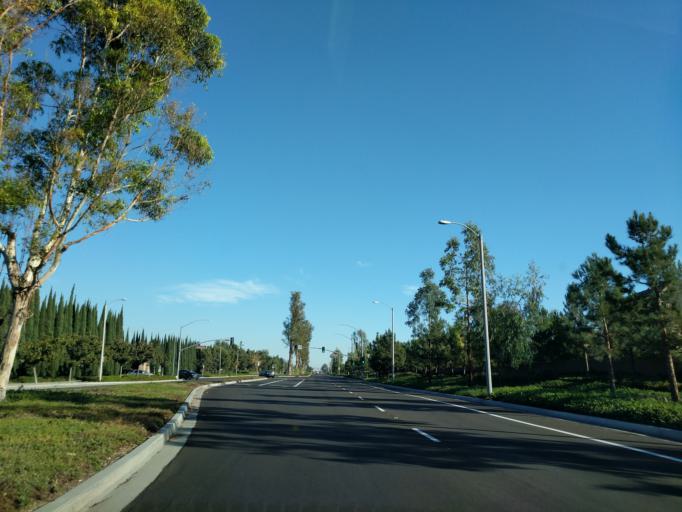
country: US
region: California
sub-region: Orange County
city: Irvine
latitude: 33.6913
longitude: -117.7550
